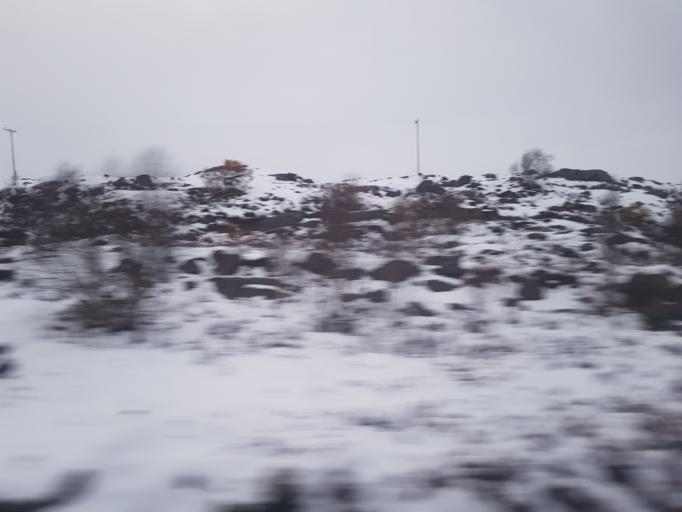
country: NO
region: Sor-Trondelag
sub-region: Oppdal
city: Oppdal
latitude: 62.2765
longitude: 9.5850
